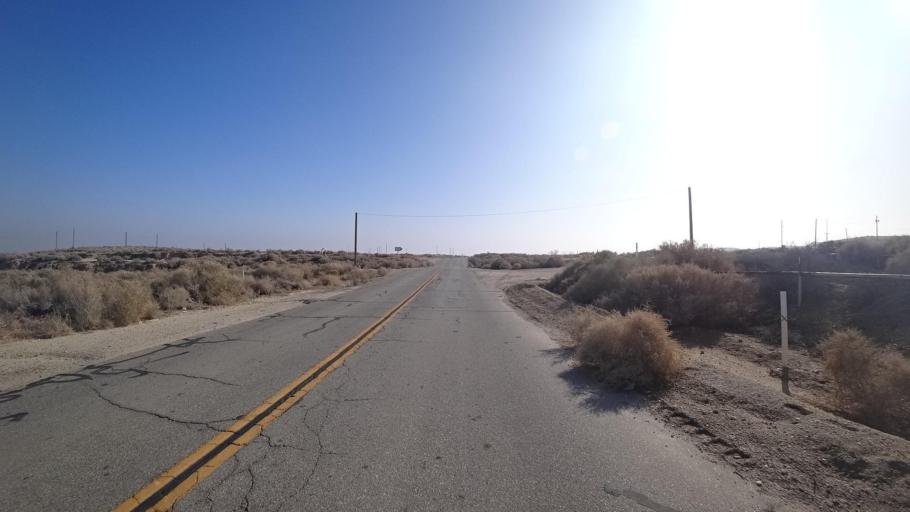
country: US
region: California
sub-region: Kern County
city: Taft Heights
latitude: 35.1630
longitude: -119.5277
